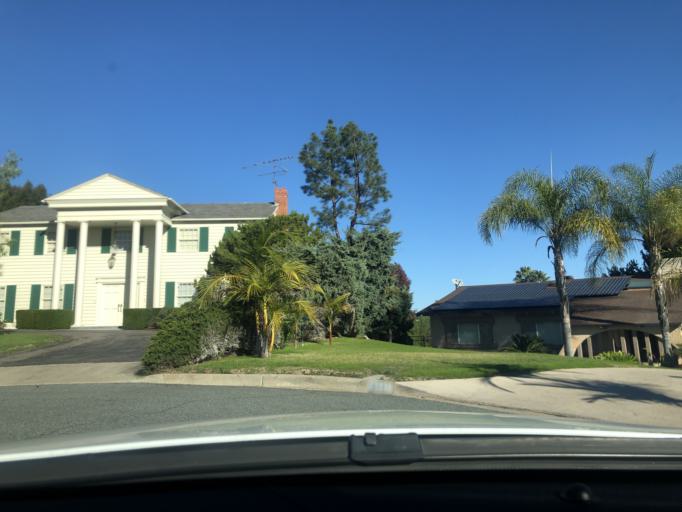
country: US
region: California
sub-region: San Diego County
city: Rancho San Diego
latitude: 32.7700
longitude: -116.9407
